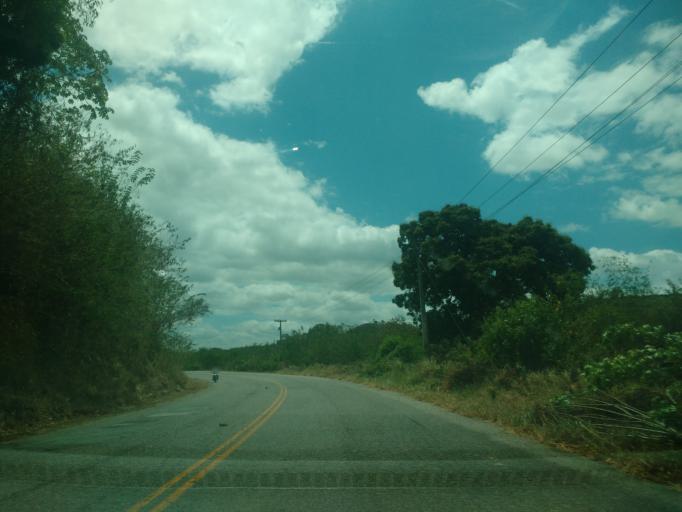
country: BR
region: Alagoas
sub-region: Santana Do Mundau
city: Santana do Mundau
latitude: -9.1453
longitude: -36.1701
